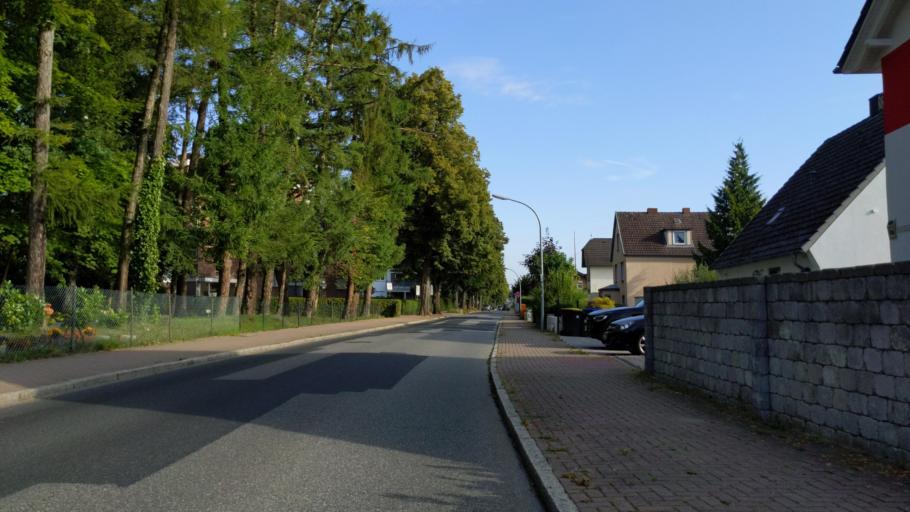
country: DE
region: Schleswig-Holstein
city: Bad Schwartau
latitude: 53.9248
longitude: 10.6929
